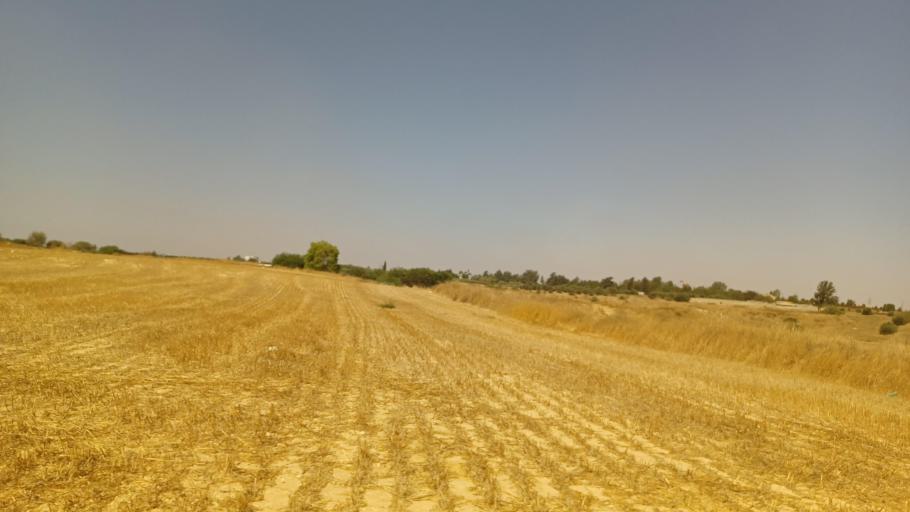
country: CY
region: Ammochostos
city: Acheritou
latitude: 35.0726
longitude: 33.8675
